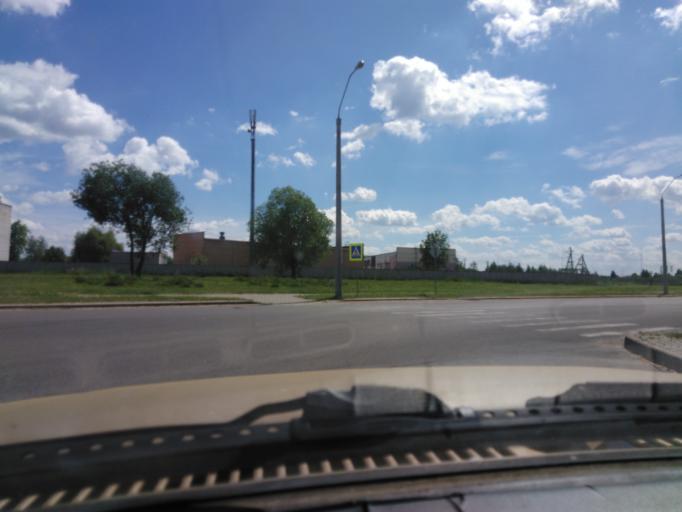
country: BY
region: Mogilev
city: Mahilyow
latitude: 53.9138
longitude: 30.2865
